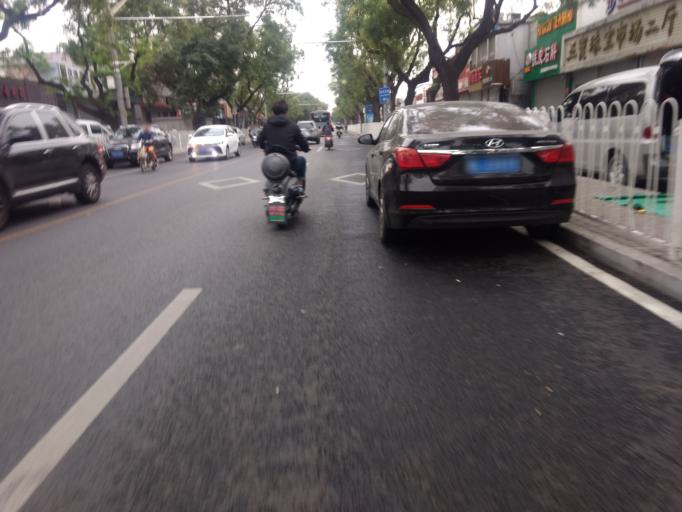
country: CN
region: Beijing
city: Jinrongjie
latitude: 39.9366
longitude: 116.3666
